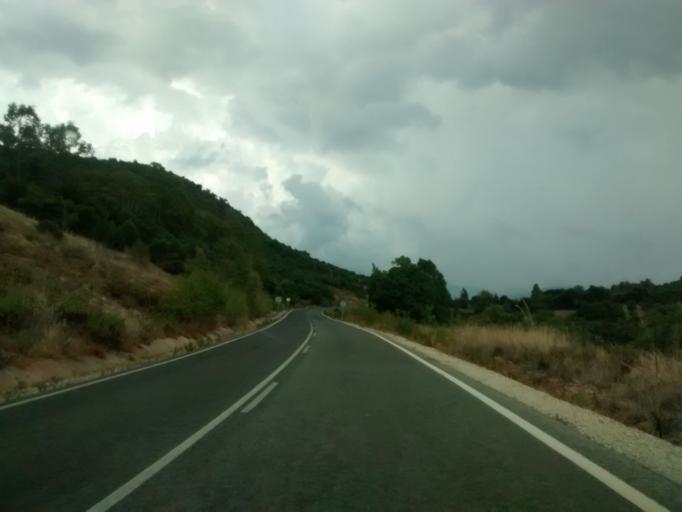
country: ES
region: Andalusia
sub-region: Provincia de Cadiz
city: Prado del Rey
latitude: 36.7989
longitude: -5.5721
